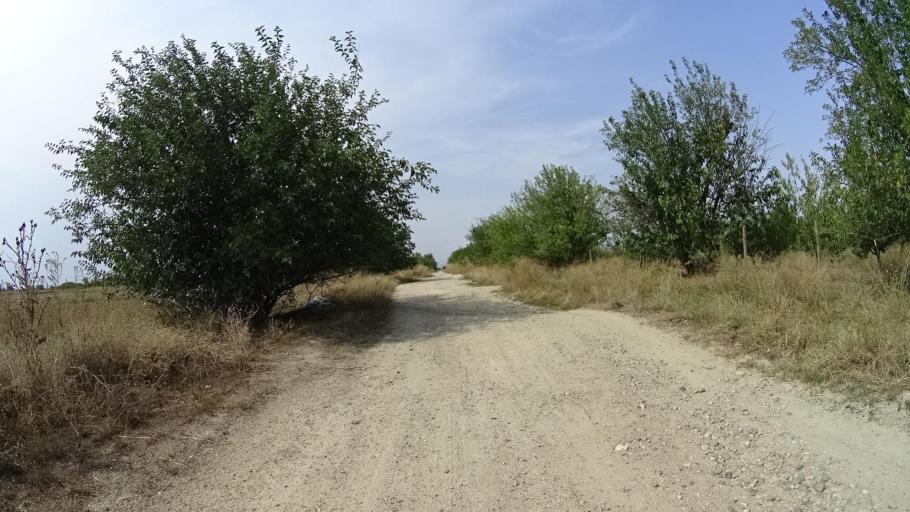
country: BG
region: Plovdiv
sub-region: Obshtina Kaloyanovo
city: Kaloyanovo
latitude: 42.2770
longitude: 24.8000
